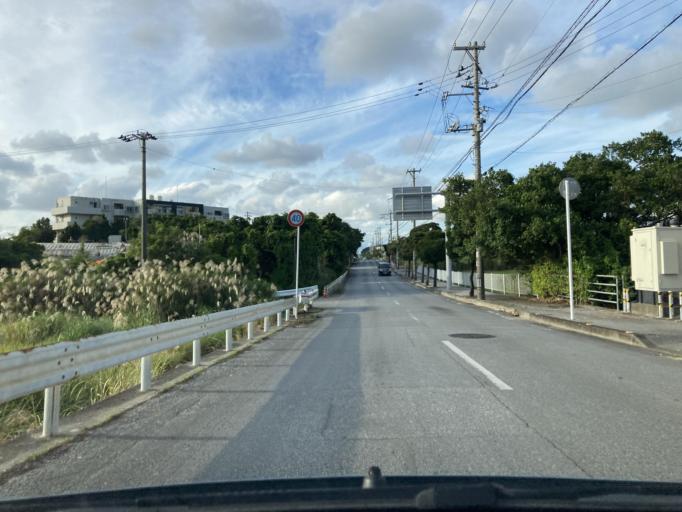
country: JP
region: Okinawa
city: Itoman
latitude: 26.1402
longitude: 127.7360
